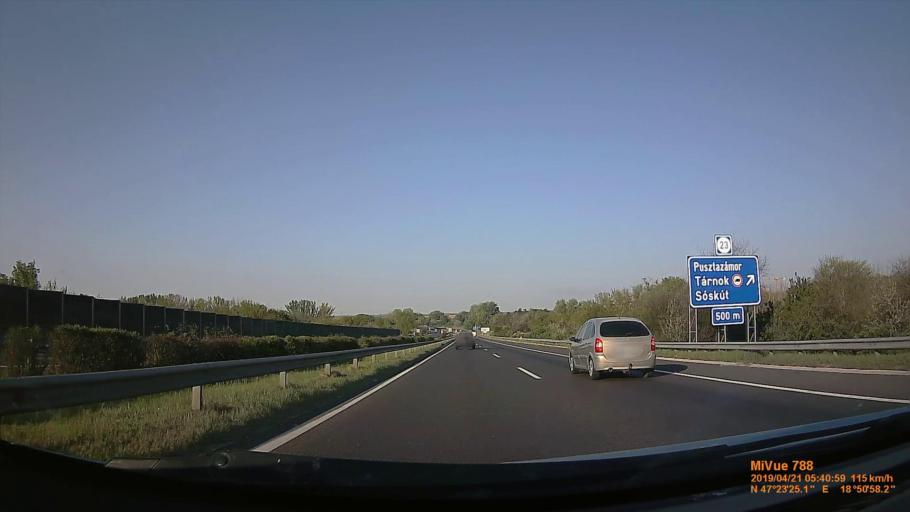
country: HU
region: Pest
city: Tarnok
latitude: 47.3902
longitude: 18.8487
